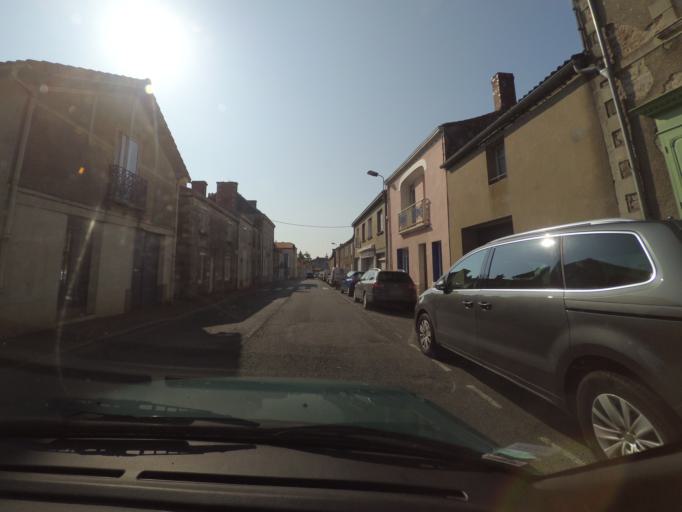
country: FR
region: Pays de la Loire
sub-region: Departement de la Loire-Atlantique
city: Le Pallet
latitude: 47.1375
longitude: -1.3343
